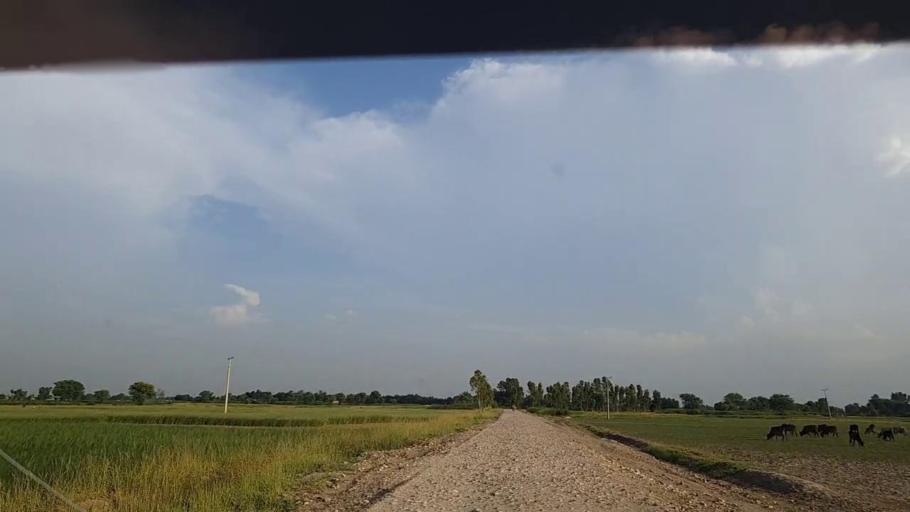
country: PK
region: Sindh
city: Khanpur
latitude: 27.8119
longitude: 69.3372
